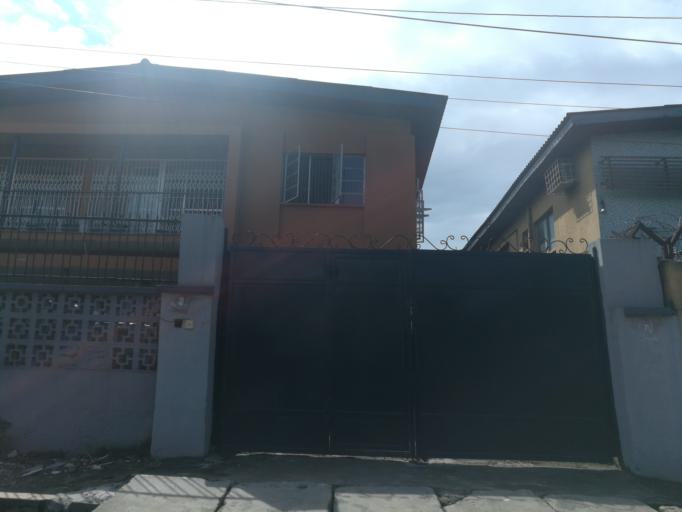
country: NG
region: Lagos
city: Somolu
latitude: 6.5481
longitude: 3.3786
